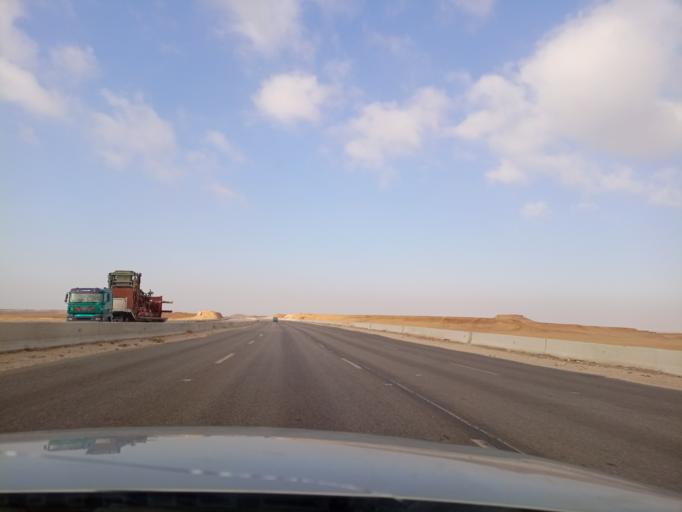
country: EG
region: Al Jizah
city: Al `Ayyat
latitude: 29.6705
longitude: 31.1909
